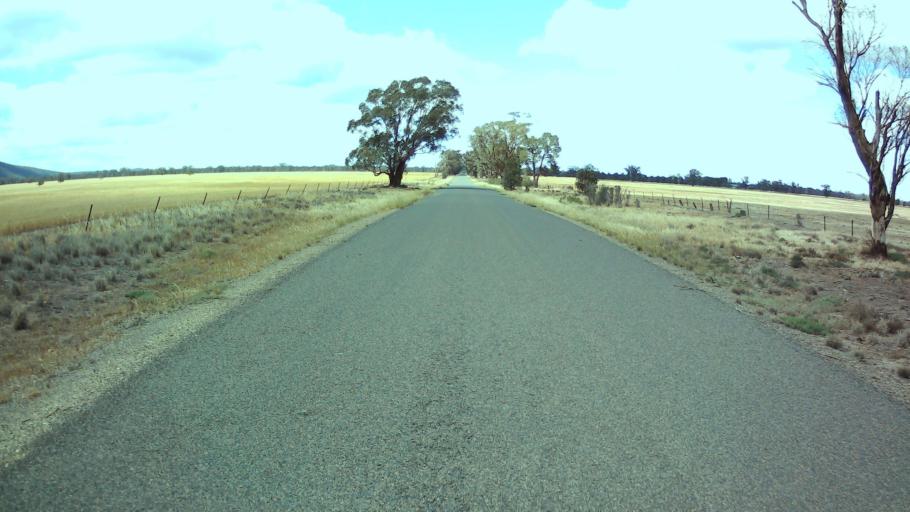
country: AU
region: New South Wales
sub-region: Weddin
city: Grenfell
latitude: -33.8814
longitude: 147.9244
